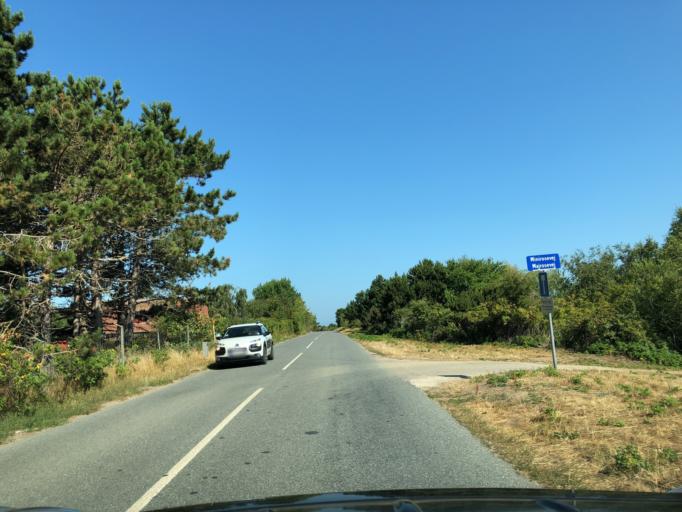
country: DK
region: Zealand
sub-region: Odsherred Kommune
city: Asnaes
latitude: 55.9878
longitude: 11.2984
